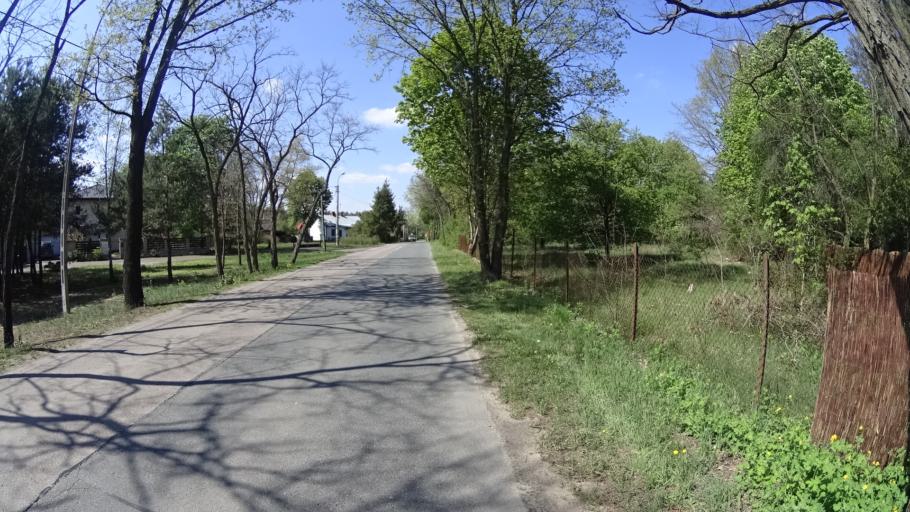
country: PL
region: Masovian Voivodeship
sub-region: Powiat warszawski zachodni
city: Hornowek
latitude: 52.2851
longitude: 20.7996
